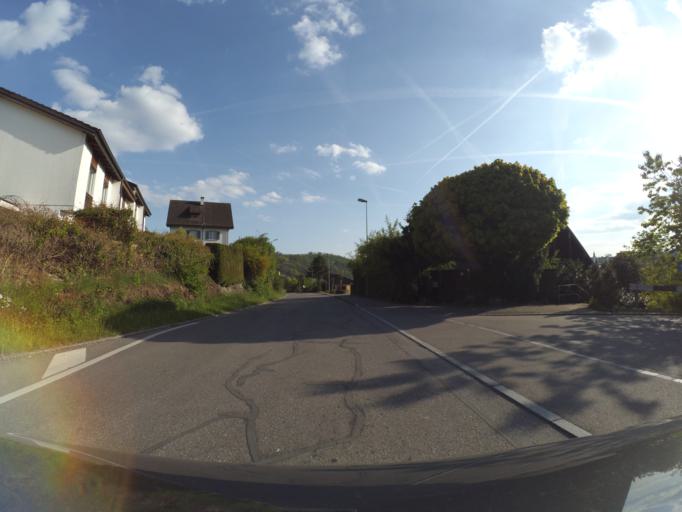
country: CH
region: Zurich
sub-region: Bezirk Andelfingen
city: Flurlingen
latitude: 47.6863
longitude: 8.6295
